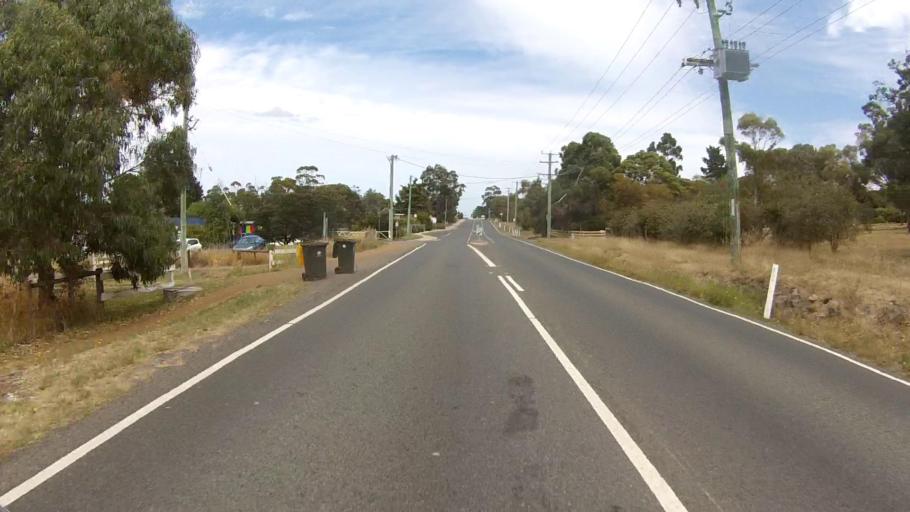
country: AU
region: Tasmania
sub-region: Clarence
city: Lauderdale
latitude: -42.9022
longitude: 147.4785
